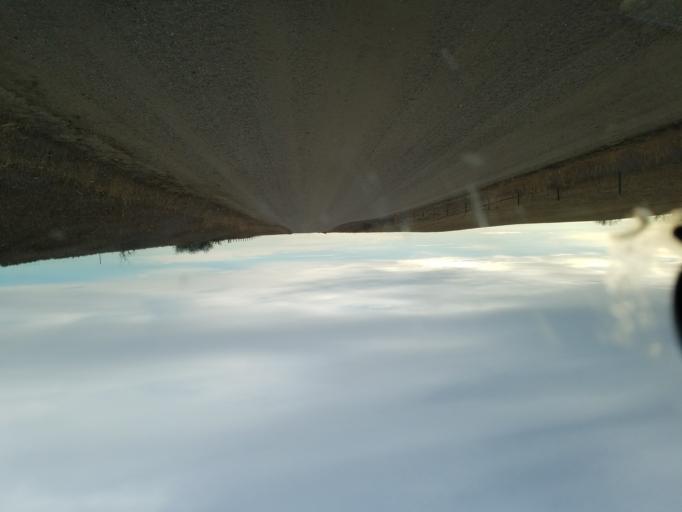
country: US
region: Nebraska
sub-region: Knox County
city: Bloomfield
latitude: 42.5460
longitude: -97.7597
